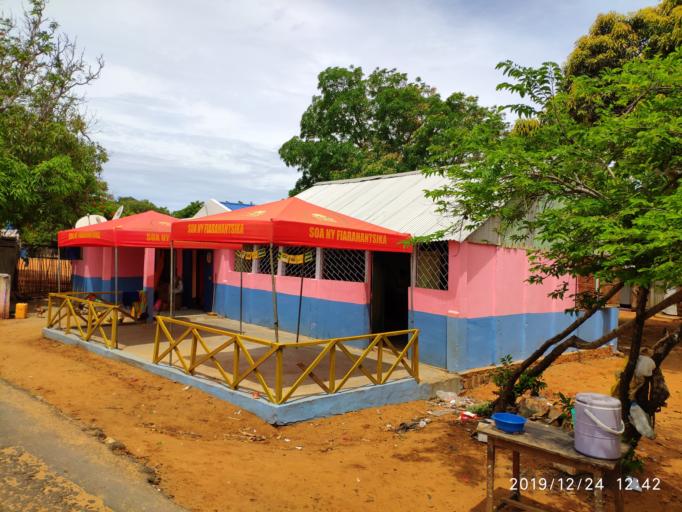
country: MG
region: Diana
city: Antsiranana
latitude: -12.2826
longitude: 49.3591
